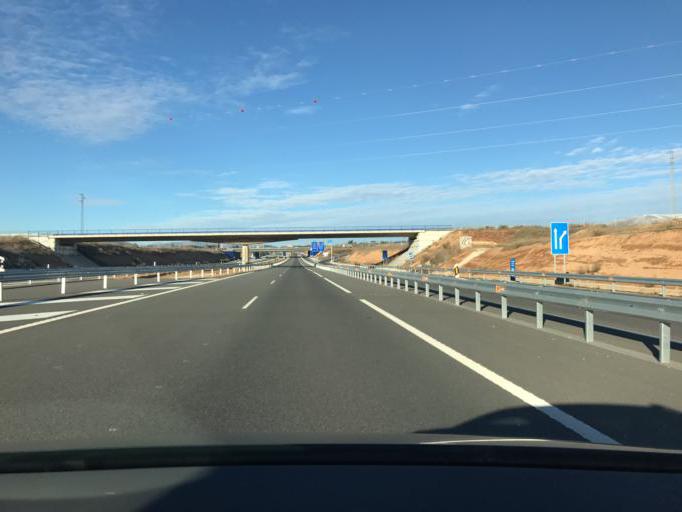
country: ES
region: Andalusia
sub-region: Provincia de Granada
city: Albolote
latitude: 37.2289
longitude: -3.6664
